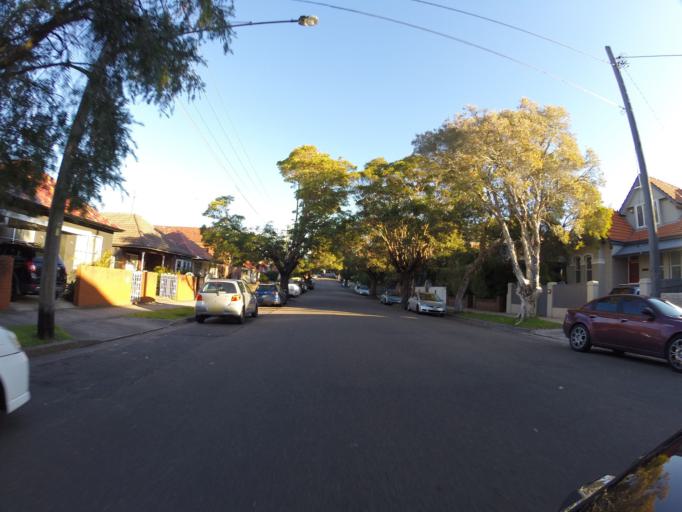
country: AU
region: New South Wales
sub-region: Waverley
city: Bondi
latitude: -33.8959
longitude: 151.2621
